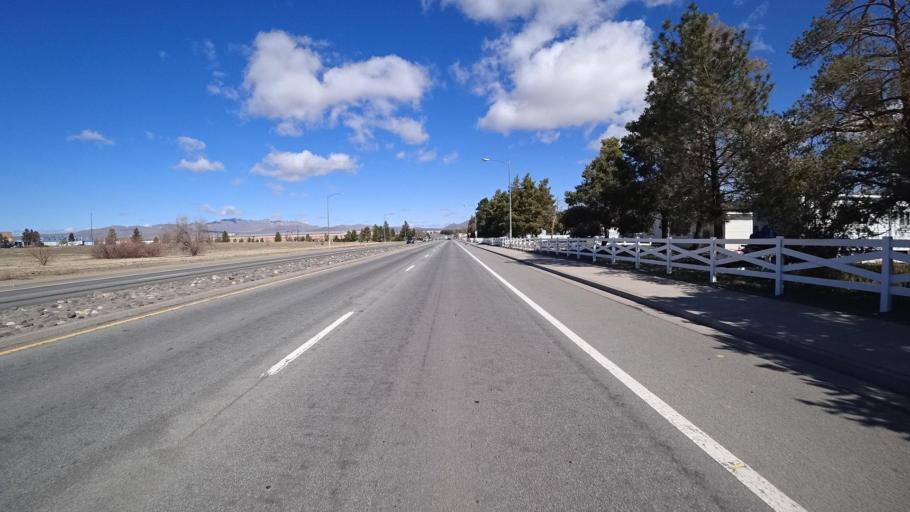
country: US
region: Nevada
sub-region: Washoe County
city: Lemmon Valley
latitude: 39.6375
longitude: -119.8817
